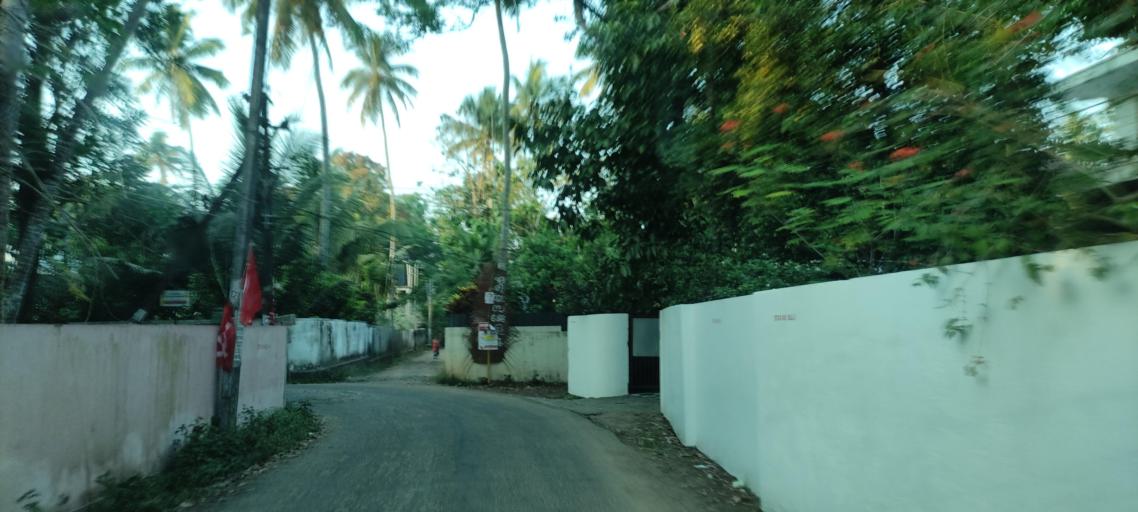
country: IN
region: Kerala
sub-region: Alappuzha
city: Kutiatodu
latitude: 9.7869
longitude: 76.3240
